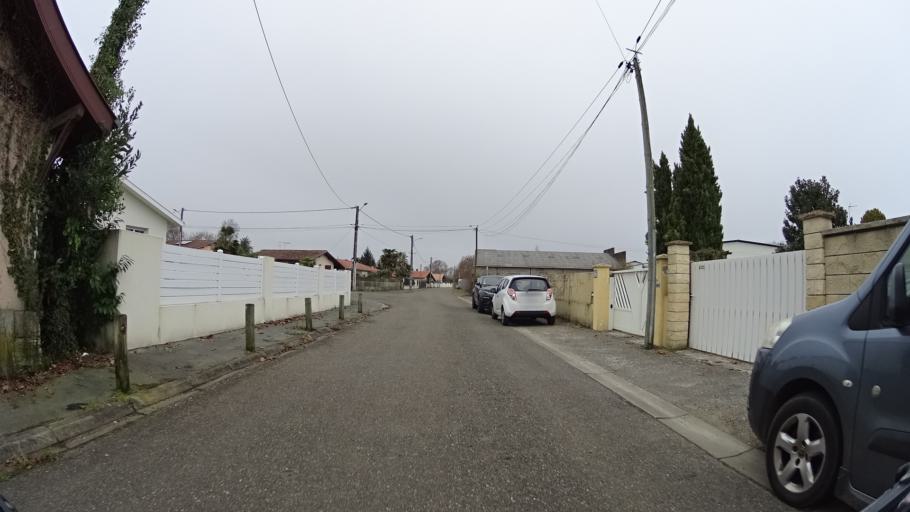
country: FR
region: Aquitaine
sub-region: Departement des Landes
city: Saint-Paul-les-Dax
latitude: 43.7320
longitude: -1.0505
